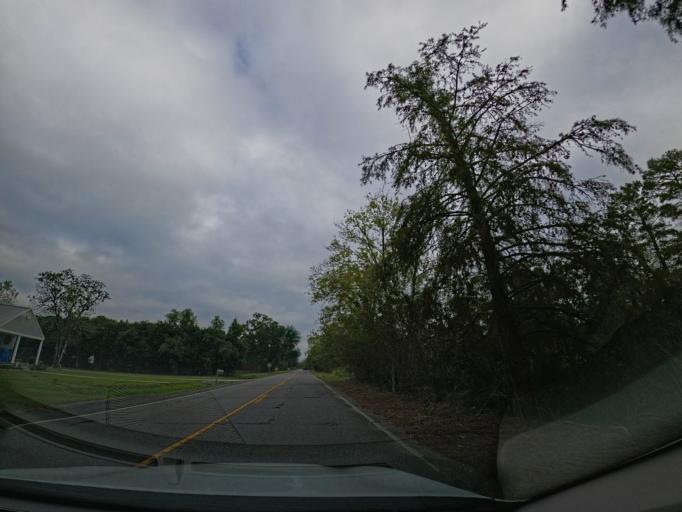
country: US
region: Louisiana
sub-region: Saint Mary Parish
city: Amelia
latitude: 29.6707
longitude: -90.9767
